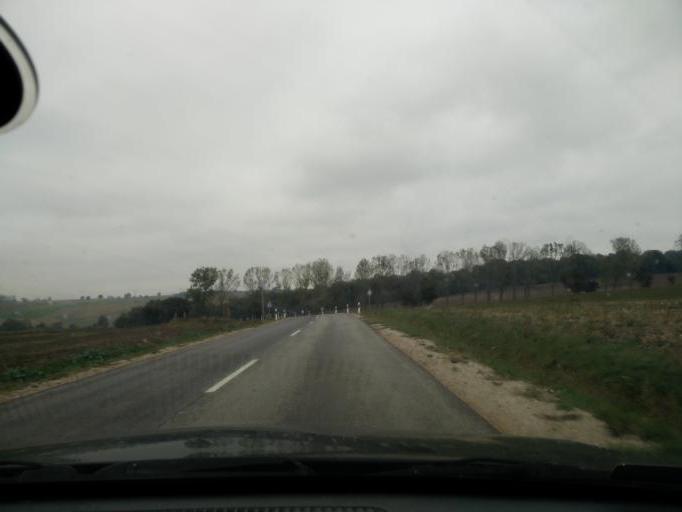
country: HU
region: Komarom-Esztergom
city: Bajna
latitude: 47.6519
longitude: 18.5800
